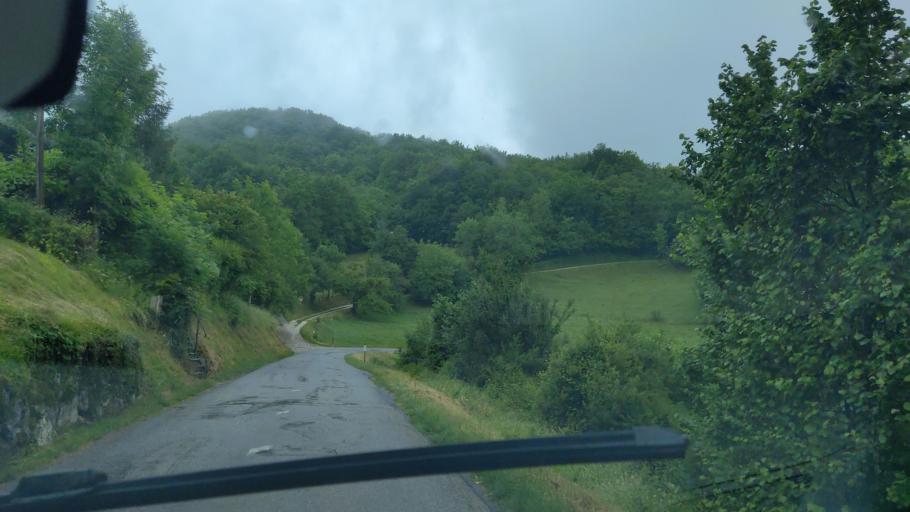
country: FR
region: Rhone-Alpes
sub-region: Departement de la Savoie
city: Chatillon
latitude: 45.7787
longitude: 5.8750
